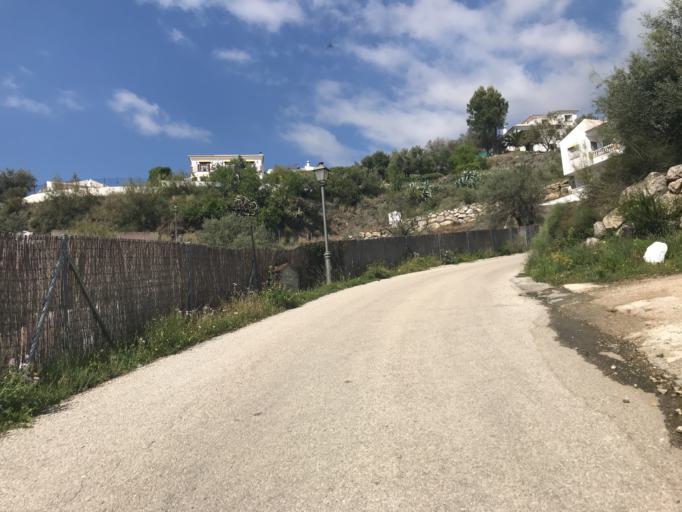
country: ES
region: Andalusia
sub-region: Provincia de Malaga
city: Alcaucin
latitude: 36.9095
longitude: -4.1101
